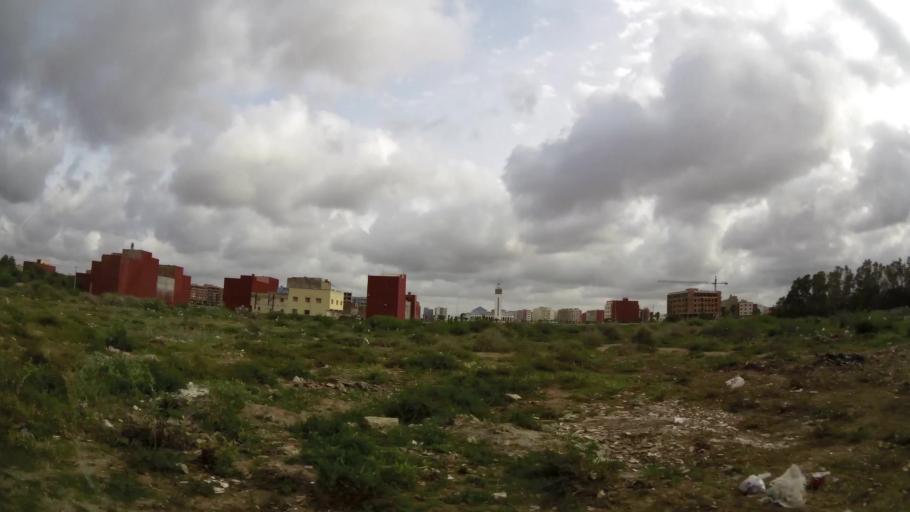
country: MA
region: Oriental
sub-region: Nador
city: Nador
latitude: 35.1568
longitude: -2.9176
